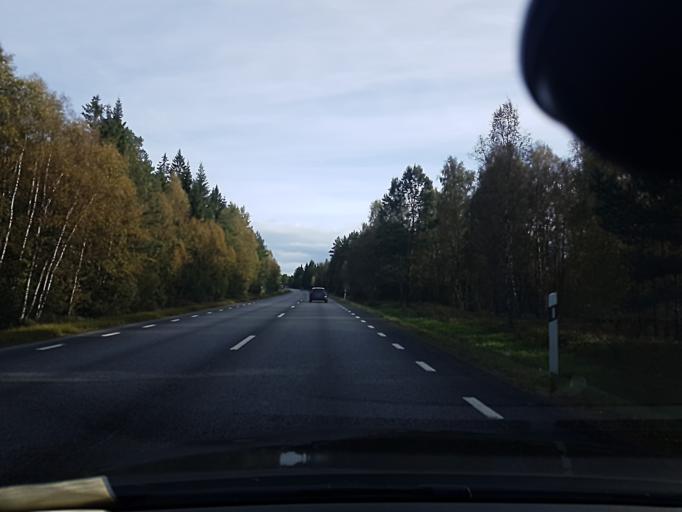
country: SE
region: Joenkoeping
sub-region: Varnamo Kommun
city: Varnamo
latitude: 57.1490
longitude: 14.0935
